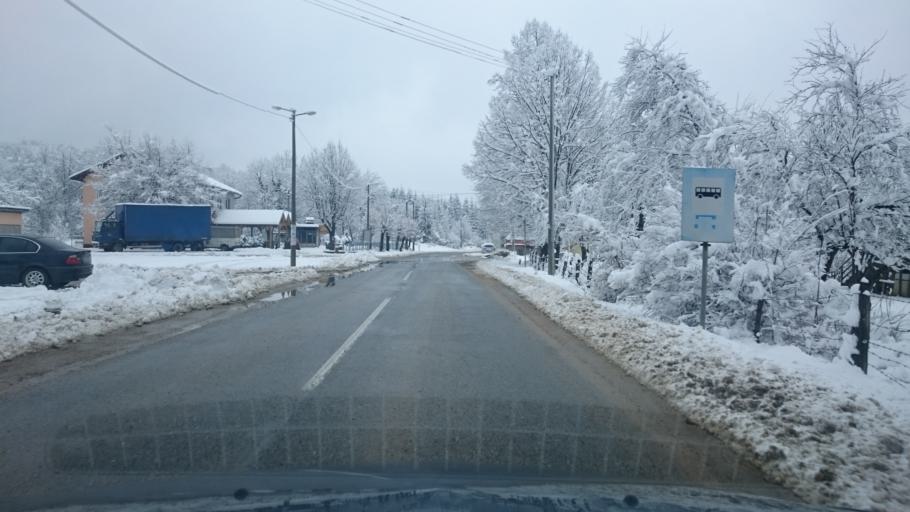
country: BA
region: Republika Srpska
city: Kotor-Varos
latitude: 44.5997
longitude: 17.2278
